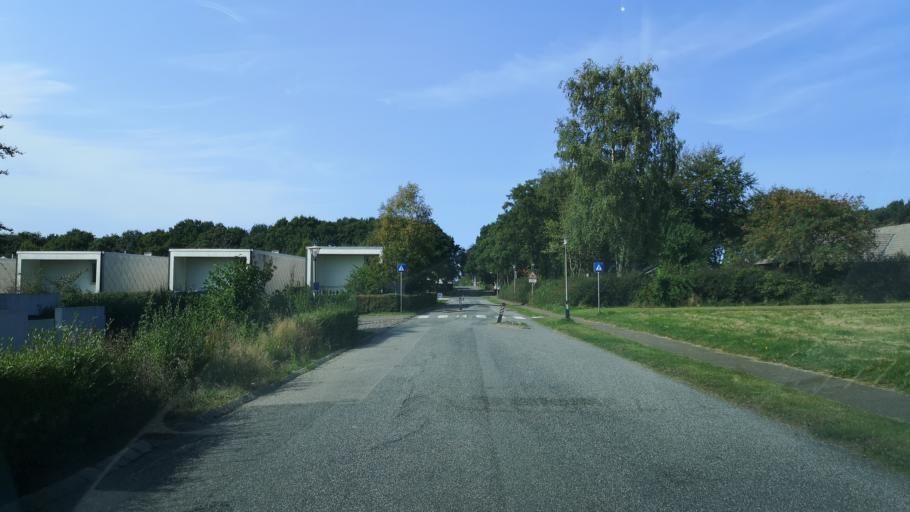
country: DK
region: Central Jutland
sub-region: Herning Kommune
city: Herning
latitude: 56.1673
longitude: 8.9748
